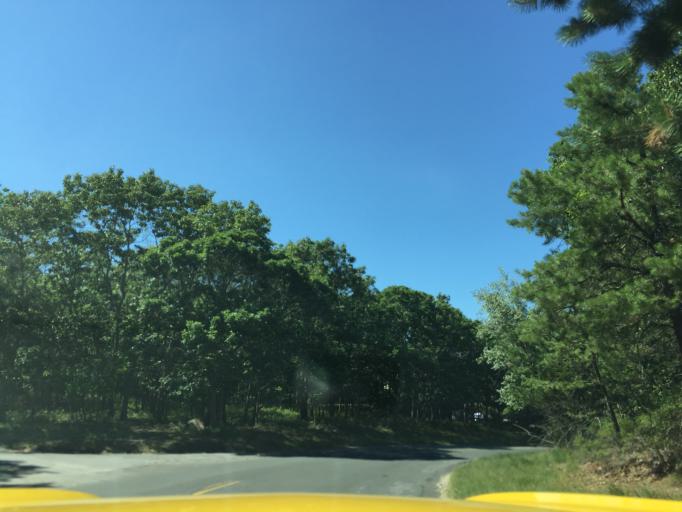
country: US
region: New York
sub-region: Suffolk County
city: Sag Harbor
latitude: 40.9746
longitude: -72.2601
